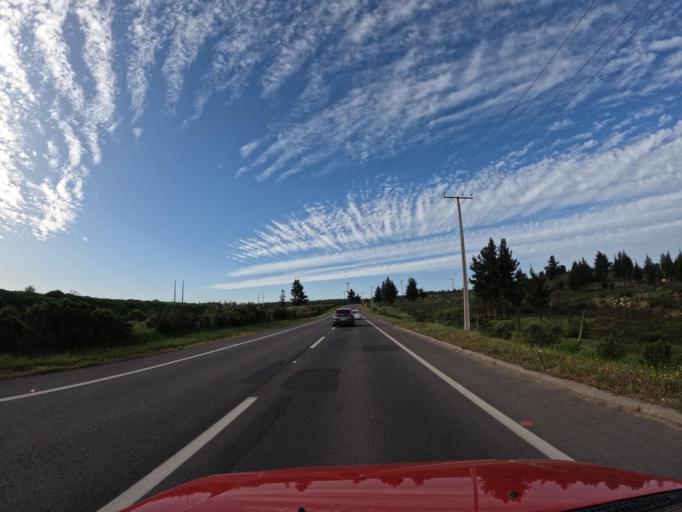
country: CL
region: Valparaiso
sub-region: San Antonio Province
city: San Antonio
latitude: -34.0592
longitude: -71.6258
